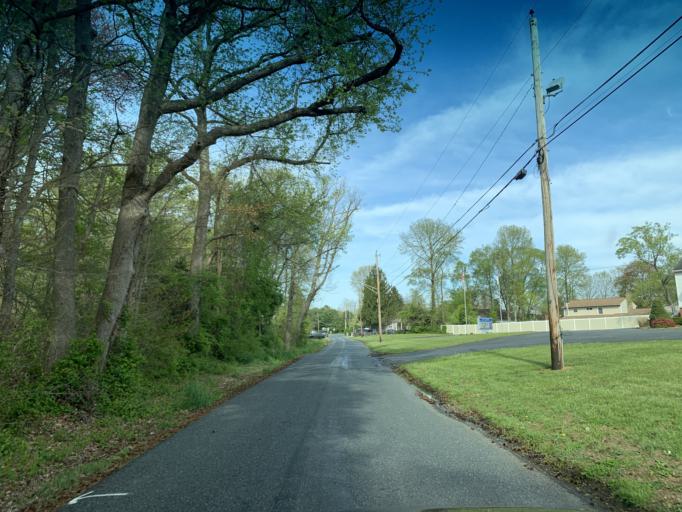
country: US
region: Maryland
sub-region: Harford County
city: Perryman
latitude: 39.4779
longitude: -76.2011
